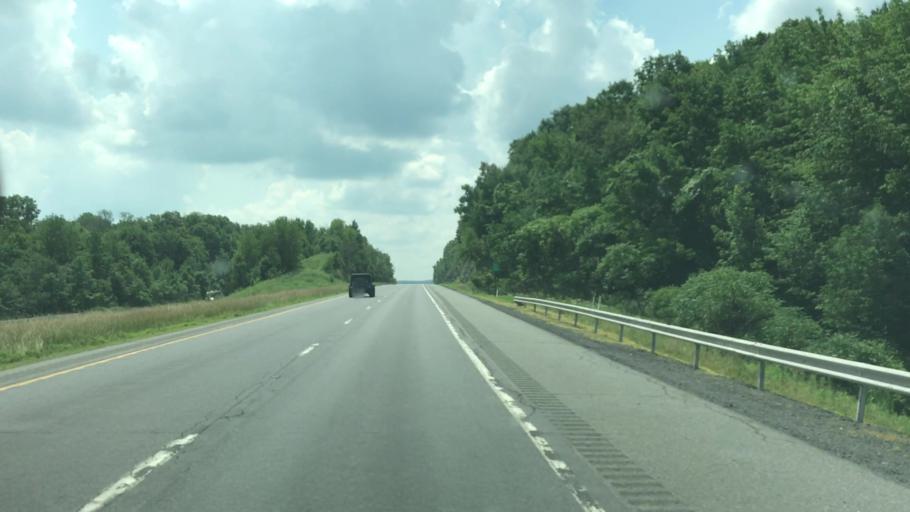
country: US
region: Pennsylvania
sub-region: Lackawanna County
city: Mount Cobb
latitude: 41.3854
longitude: -75.4596
